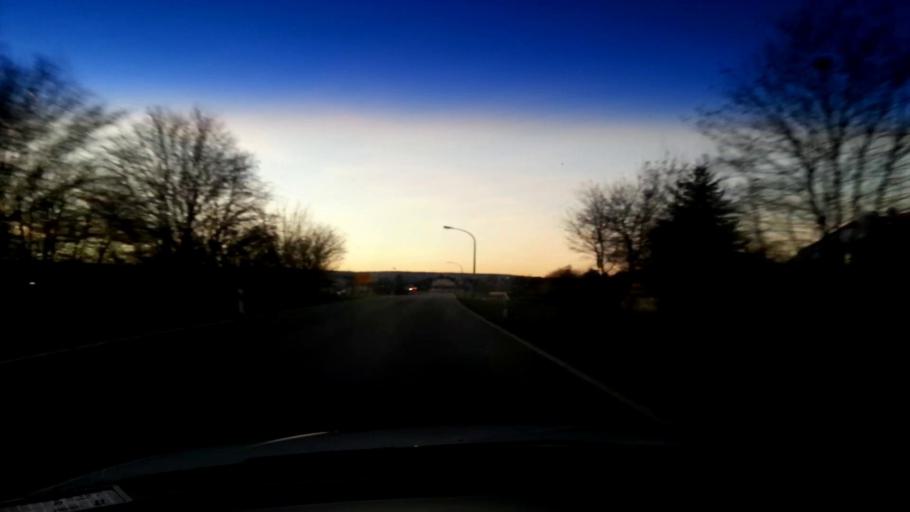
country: DE
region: Bavaria
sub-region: Upper Franconia
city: Rattelsdorf
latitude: 50.0114
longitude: 10.8998
